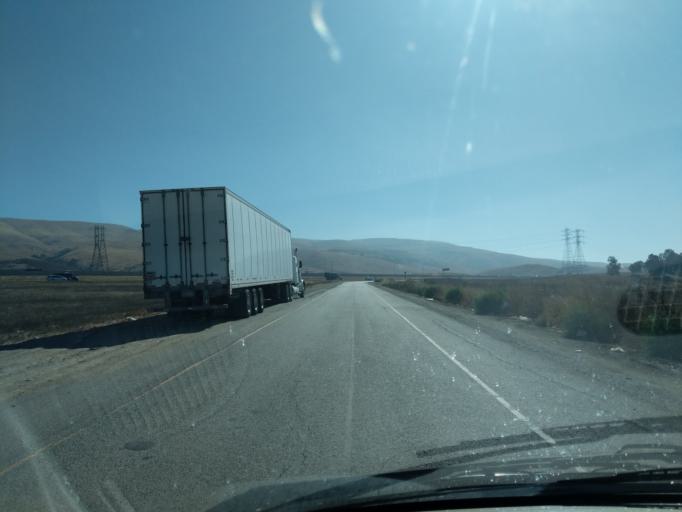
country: US
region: California
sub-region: Santa Clara County
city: Morgan Hill
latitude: 37.1890
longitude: -121.6938
